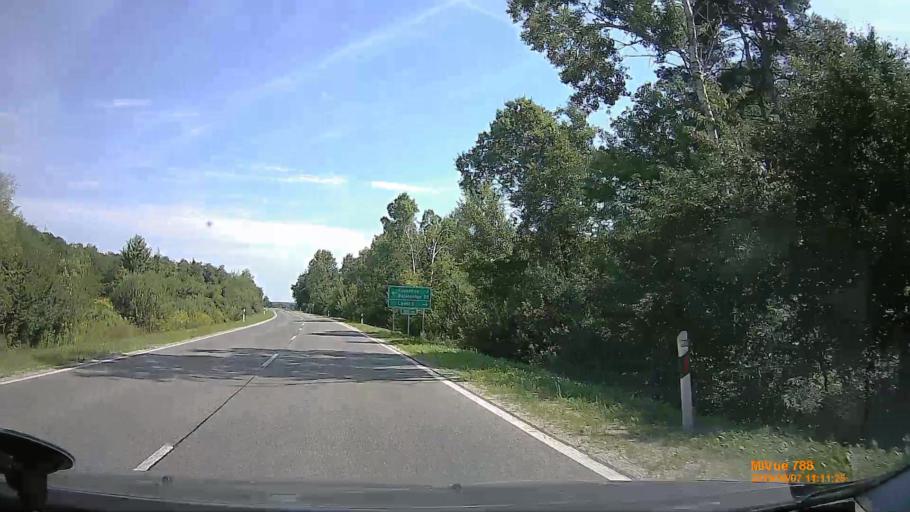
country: HU
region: Zala
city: Lenti
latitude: 46.6777
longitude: 16.5254
